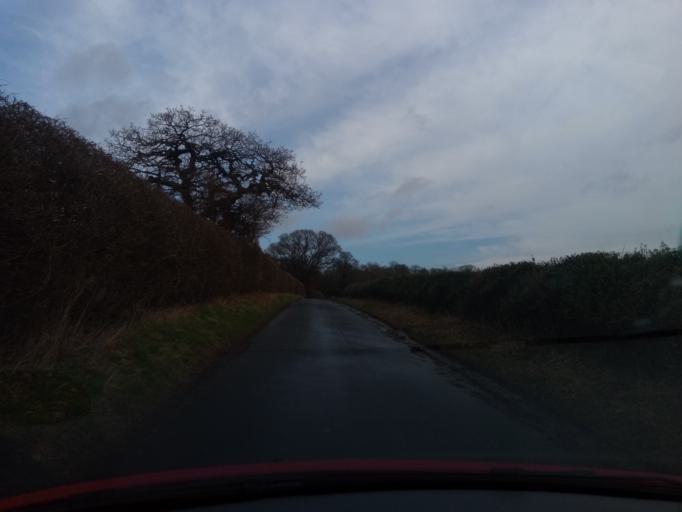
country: GB
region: England
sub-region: Northumberland
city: Corbridge
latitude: 54.9907
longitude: -2.0329
